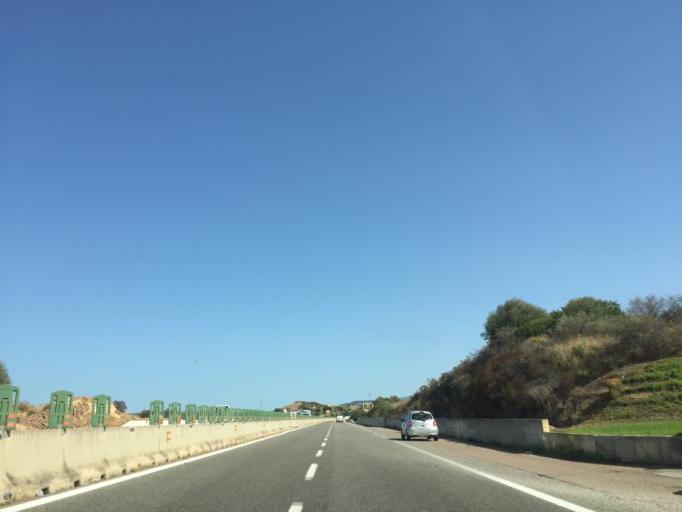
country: IT
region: Sardinia
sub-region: Provincia di Olbia-Tempio
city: Olbia
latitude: 40.8871
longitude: 9.4934
